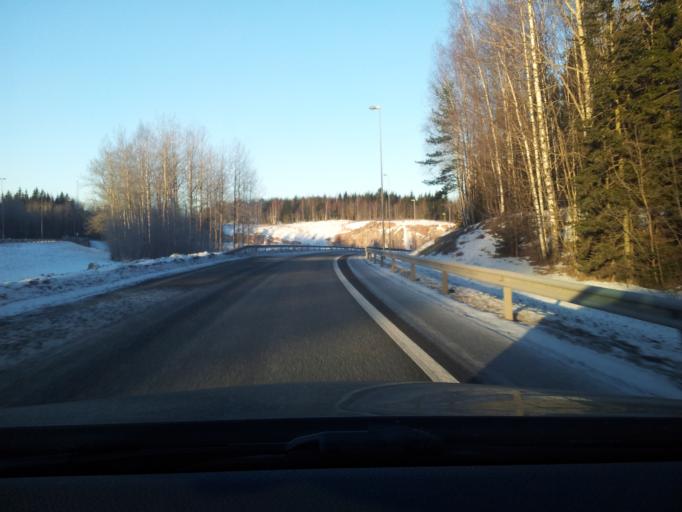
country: FI
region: Uusimaa
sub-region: Helsinki
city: Vihti
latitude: 60.2938
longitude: 24.3693
